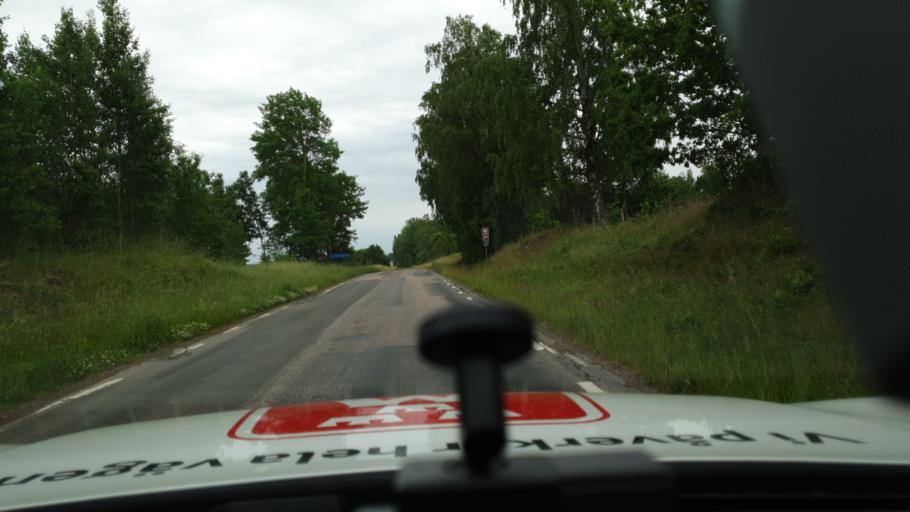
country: SE
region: Vaestra Goetaland
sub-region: Skovde Kommun
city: Stopen
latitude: 58.5249
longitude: 13.8643
